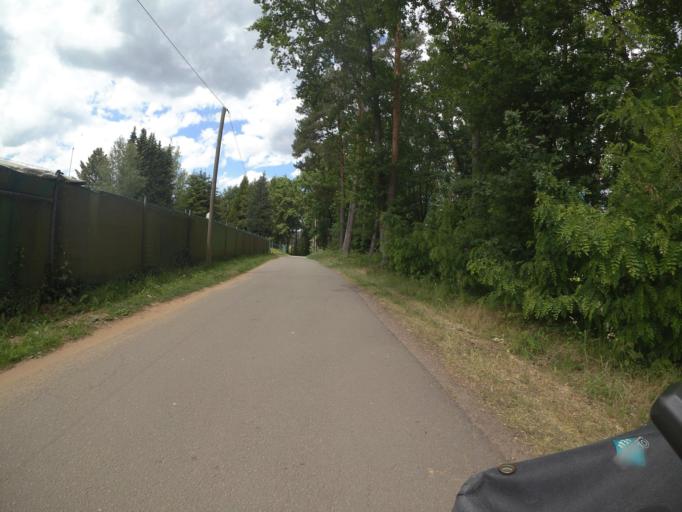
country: DE
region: Rheinland-Pfalz
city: Bruchmuhlbach-Miesau
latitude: 49.4139
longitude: 7.4449
